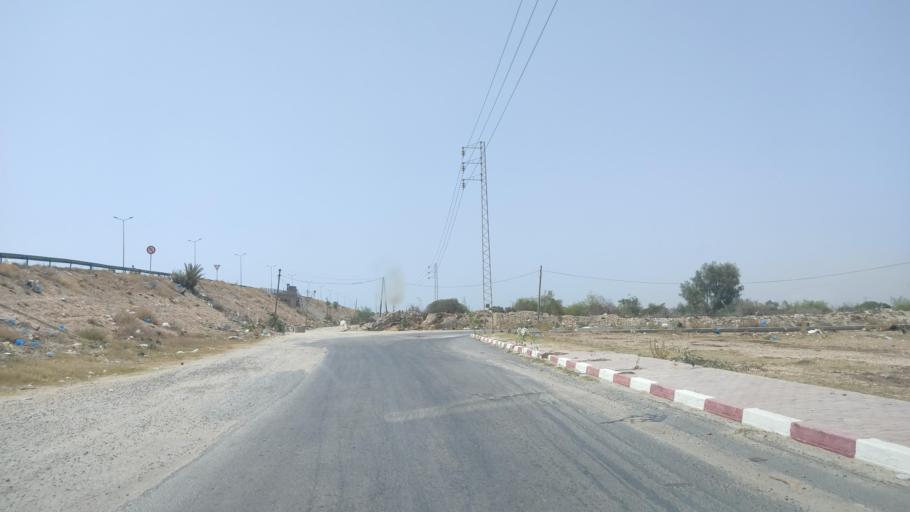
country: TN
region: Safaqis
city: Sfax
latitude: 34.7072
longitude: 10.7215
